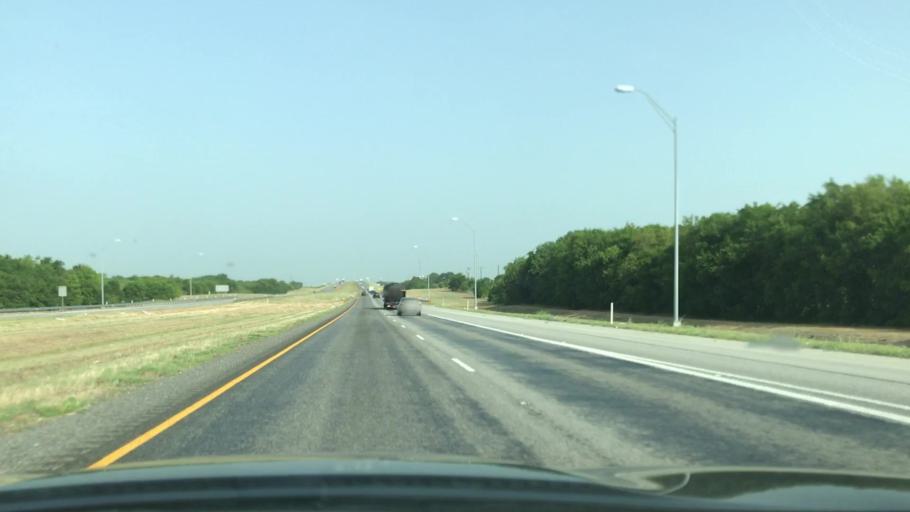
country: US
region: Texas
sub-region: Kaufman County
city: Talty
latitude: 32.7322
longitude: -96.3442
